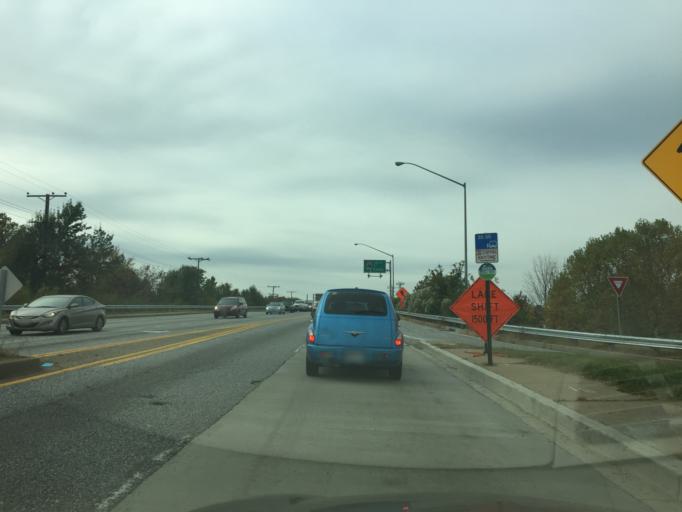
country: US
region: Maryland
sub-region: Baltimore County
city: Rossville
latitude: 39.3370
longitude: -76.4905
